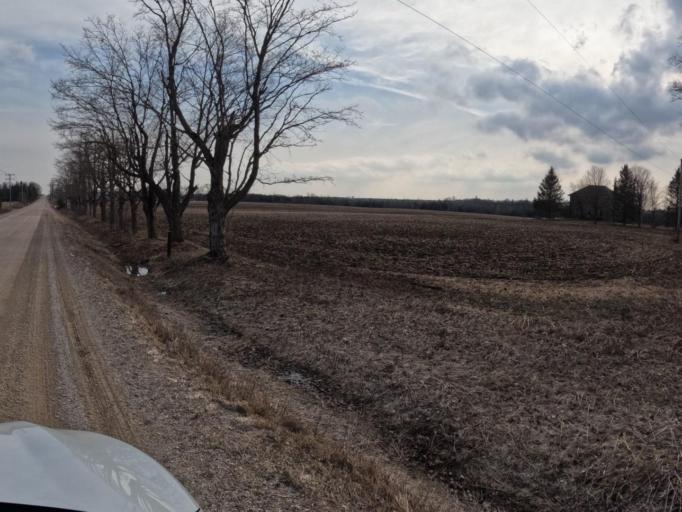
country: CA
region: Ontario
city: Shelburne
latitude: 43.9107
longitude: -80.3038
